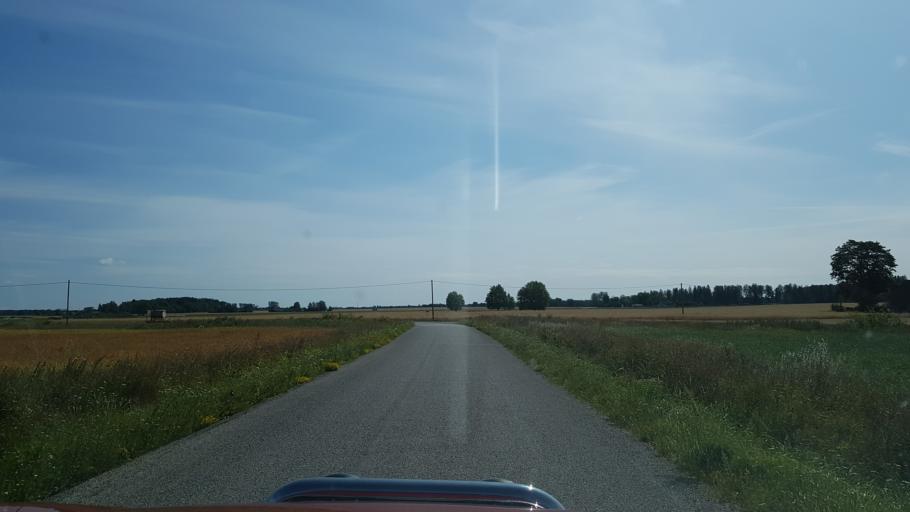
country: EE
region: Jaervamaa
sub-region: Jaerva-Jaani vald
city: Jarva-Jaani
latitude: 59.0899
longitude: 25.6993
